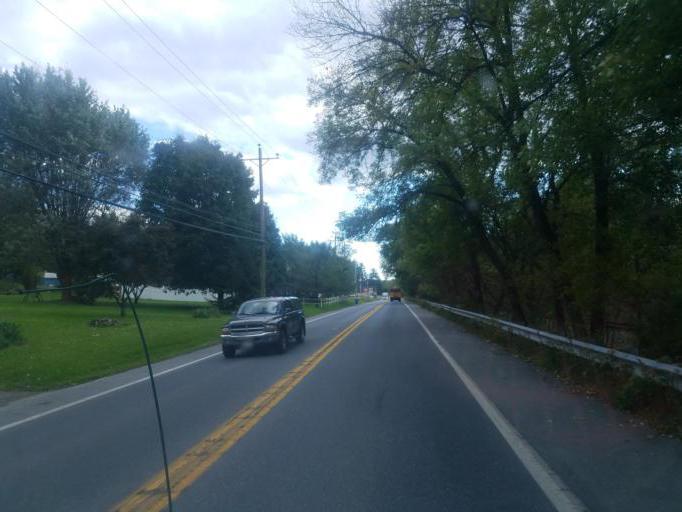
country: US
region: Pennsylvania
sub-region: Dauphin County
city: Middletown
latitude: 40.1741
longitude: -76.7237
